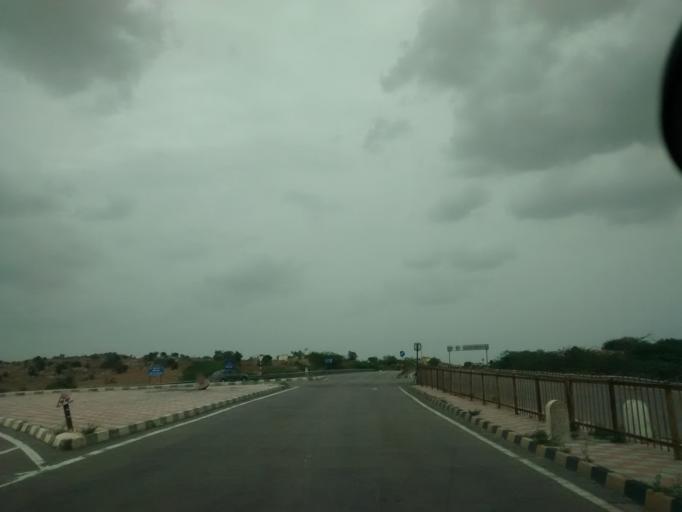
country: IN
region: Andhra Pradesh
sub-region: Kurnool
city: Ramapuram
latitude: 15.1544
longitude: 77.6673
